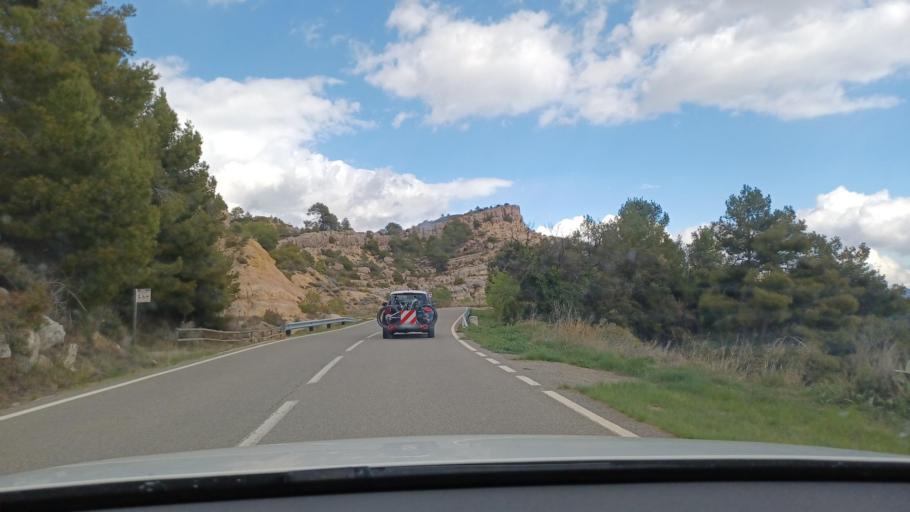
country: ES
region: Catalonia
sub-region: Provincia de Tarragona
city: la Morera de Montsant
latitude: 41.2695
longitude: 0.8513
